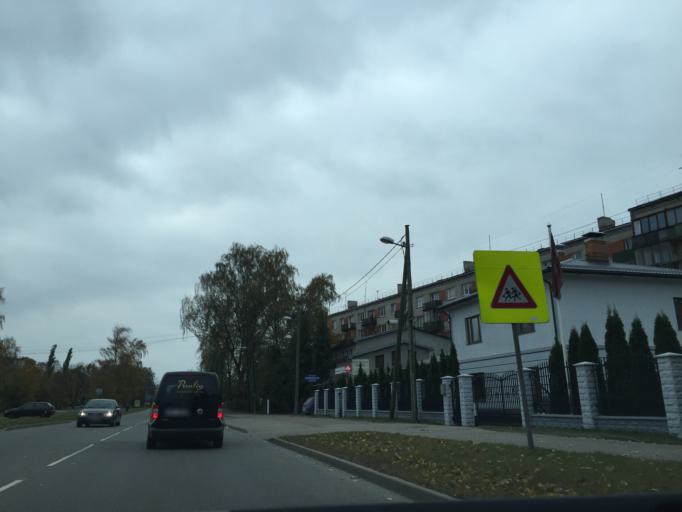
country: LV
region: Riga
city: Riga
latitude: 56.9142
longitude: 24.0966
